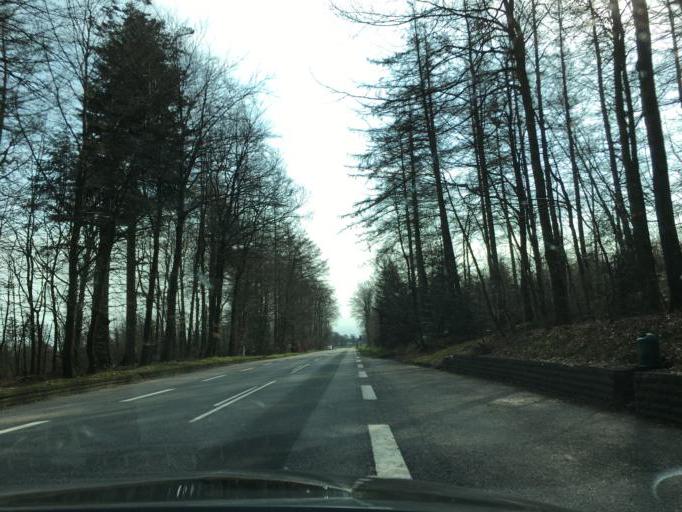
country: DK
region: South Denmark
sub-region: Vejen Kommune
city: Vejen
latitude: 55.4922
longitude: 9.0854
